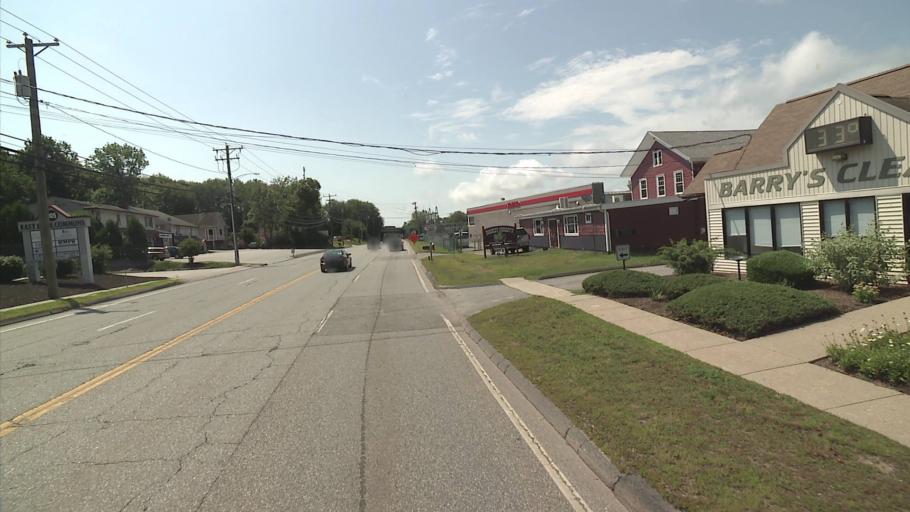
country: US
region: Connecticut
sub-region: New London County
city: Niantic
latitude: 41.3638
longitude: -72.2093
